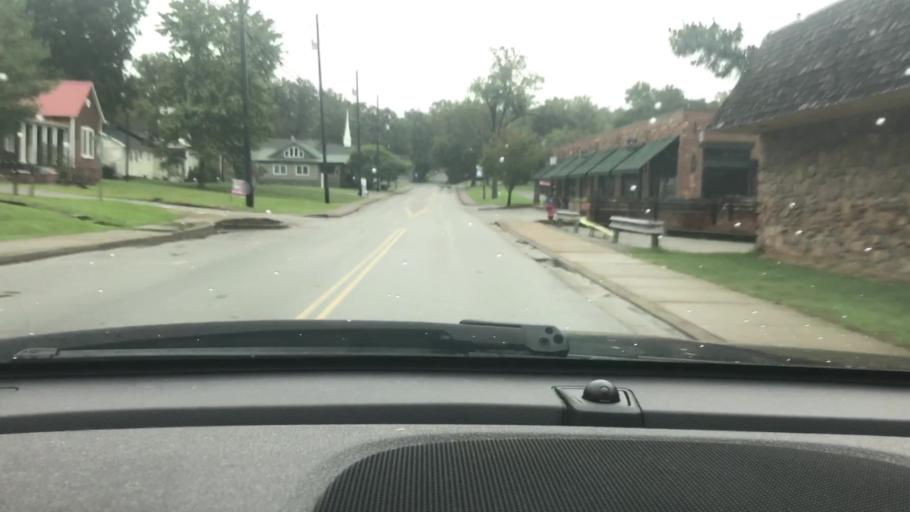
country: US
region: Tennessee
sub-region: Cheatham County
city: Kingston Springs
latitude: 36.1010
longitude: -87.1149
